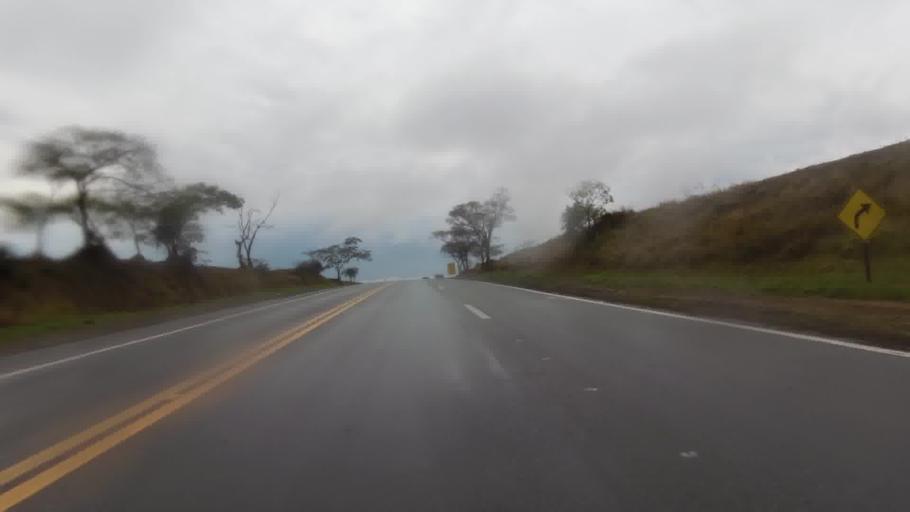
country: BR
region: Rio de Janeiro
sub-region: Campos Dos Goytacazes
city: Campos
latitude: -21.5147
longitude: -41.3339
